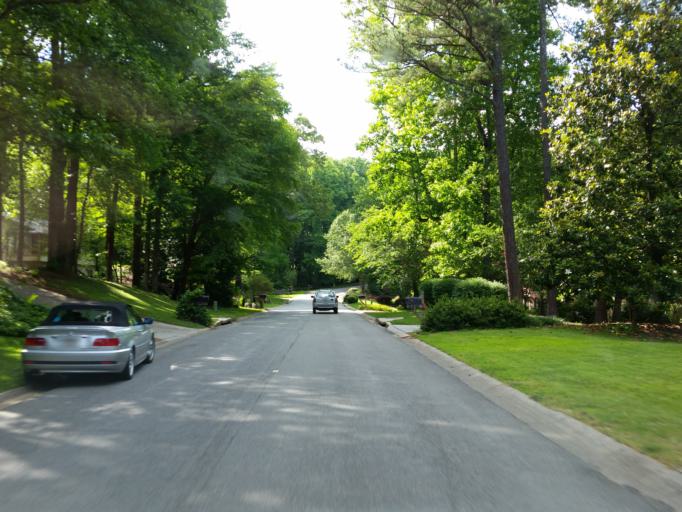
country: US
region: Georgia
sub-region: Fulton County
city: Roswell
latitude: 34.0078
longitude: -84.4202
